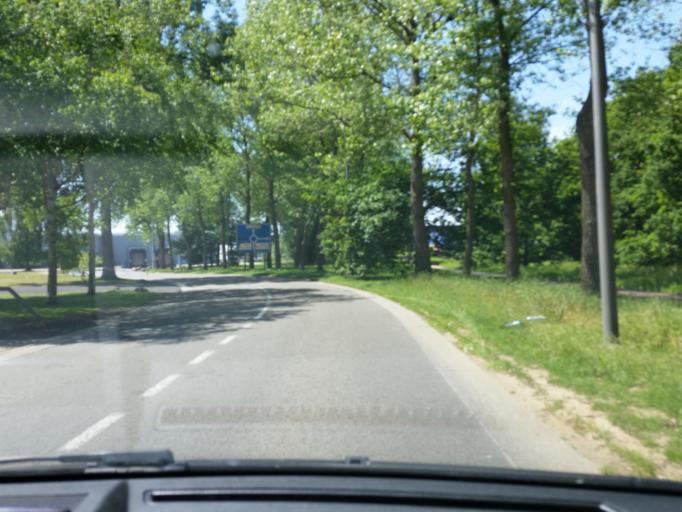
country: BE
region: Flanders
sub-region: Provincie Antwerpen
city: Mechelen
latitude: 51.0524
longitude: 4.4502
